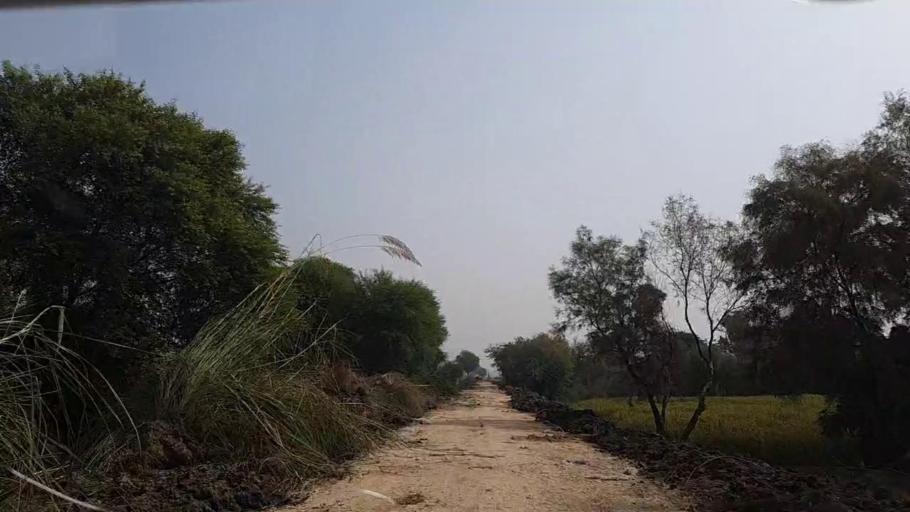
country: PK
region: Sindh
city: Shikarpur
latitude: 27.9198
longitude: 68.5823
